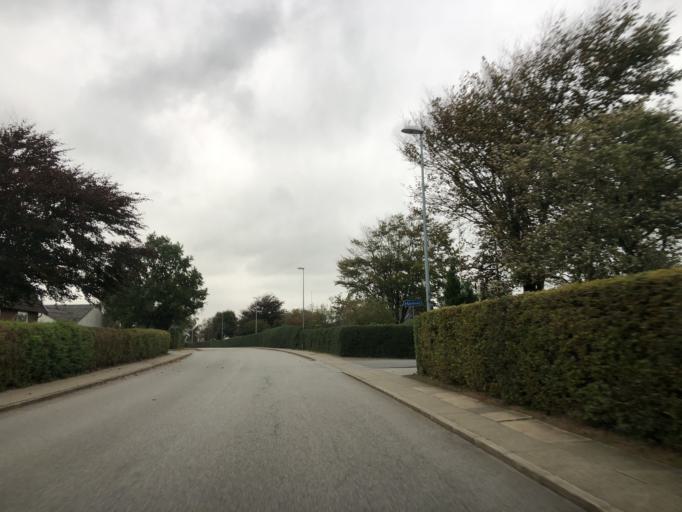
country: DK
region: Central Jutland
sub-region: Herning Kommune
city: Avlum
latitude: 56.2705
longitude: 8.7944
